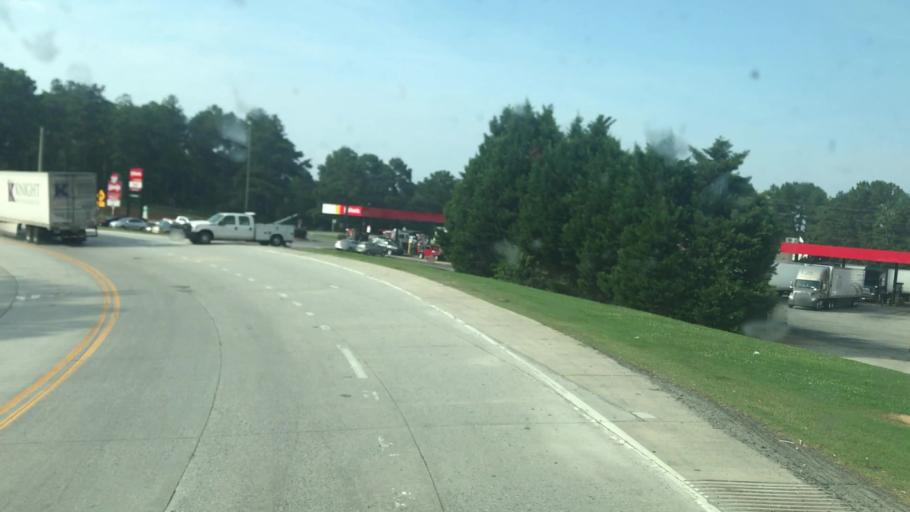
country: US
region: Georgia
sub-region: Butts County
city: Jackson
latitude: 33.2097
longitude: -84.0570
